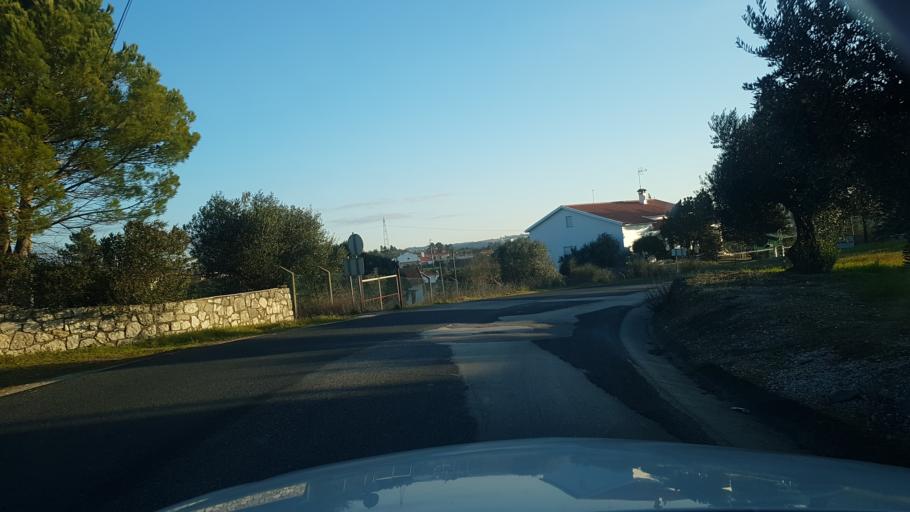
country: PT
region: Santarem
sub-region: Torres Novas
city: Torres Novas
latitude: 39.5540
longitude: -8.5615
